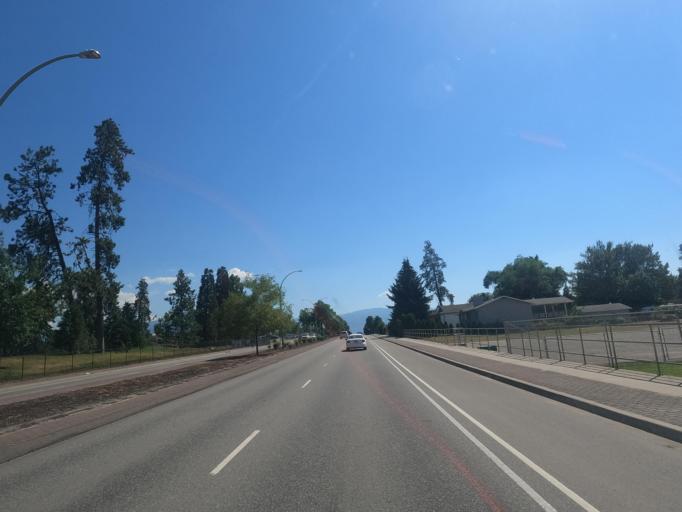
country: CA
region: British Columbia
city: Kelowna
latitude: 49.8936
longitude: -119.4546
